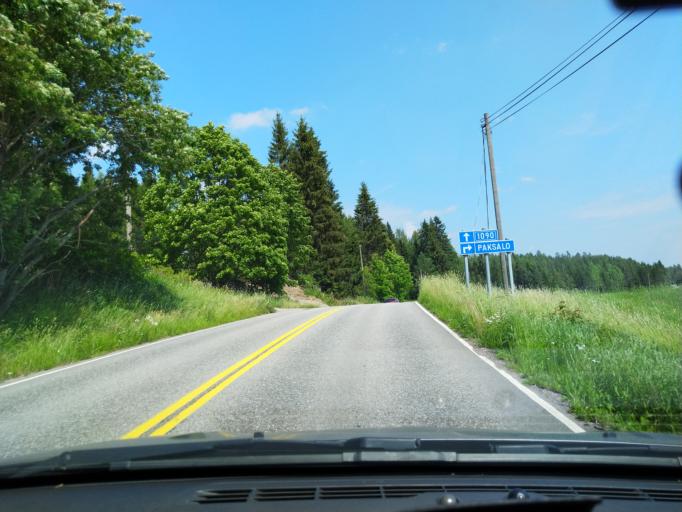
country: FI
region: Uusimaa
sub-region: Helsinki
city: Lohja
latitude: 60.3382
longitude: 24.0654
